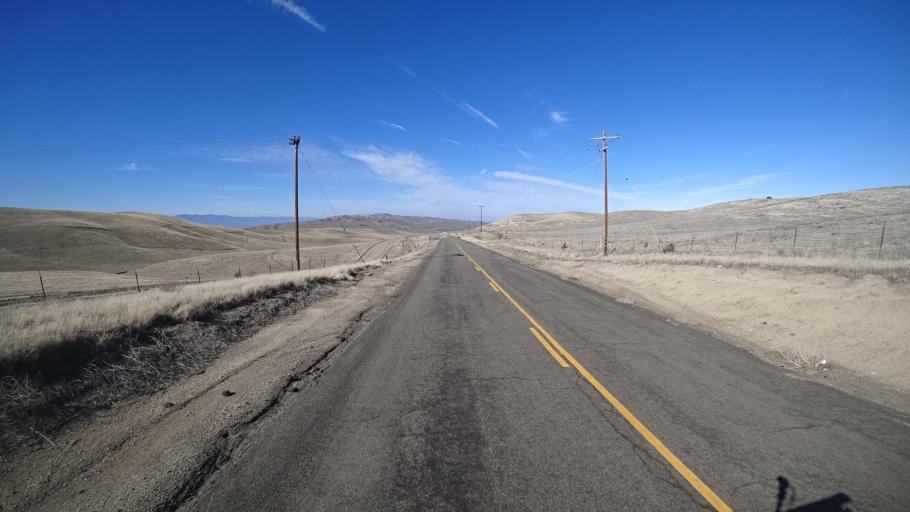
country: US
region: California
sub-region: Kern County
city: Maricopa
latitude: 34.9485
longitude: -119.4199
